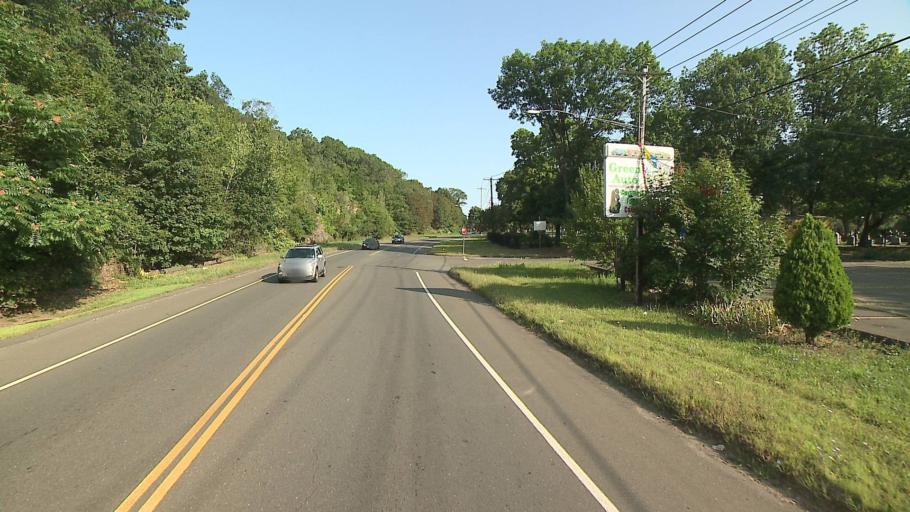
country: US
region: Connecticut
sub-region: New Haven County
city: West Haven
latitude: 41.3021
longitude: -72.9639
